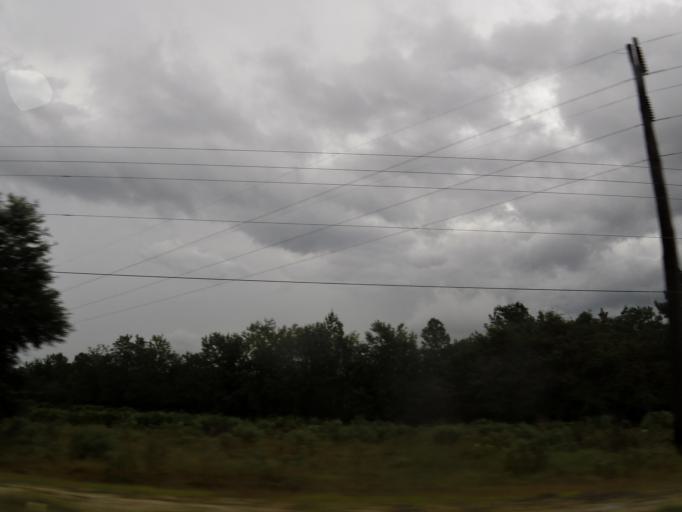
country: US
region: Georgia
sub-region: McIntosh County
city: Darien
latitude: 31.4255
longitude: -81.6696
